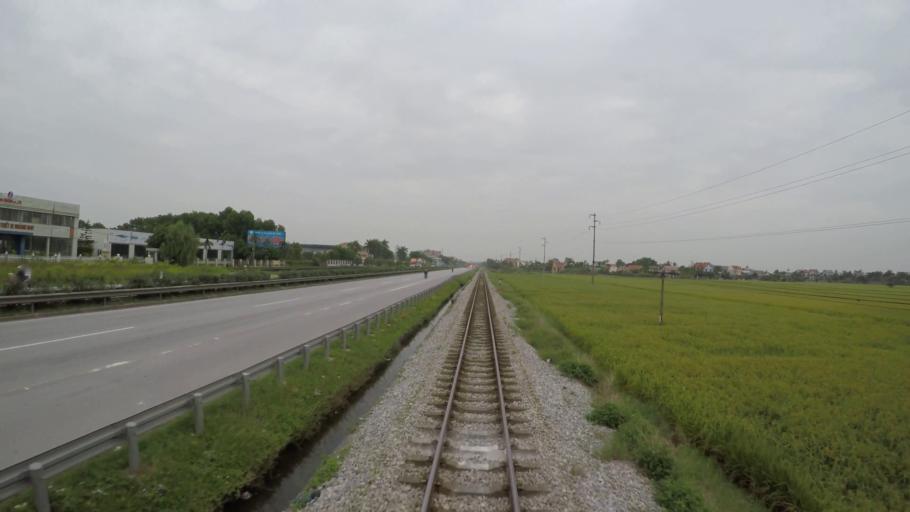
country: VN
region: Hai Duong
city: Phu Thai
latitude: 20.9704
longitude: 106.4664
